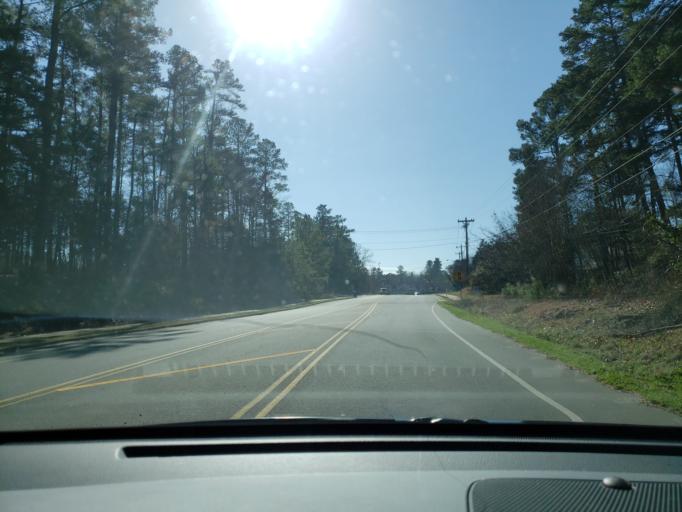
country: US
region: North Carolina
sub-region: Orange County
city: Chapel Hill
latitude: 35.9535
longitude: -79.0155
